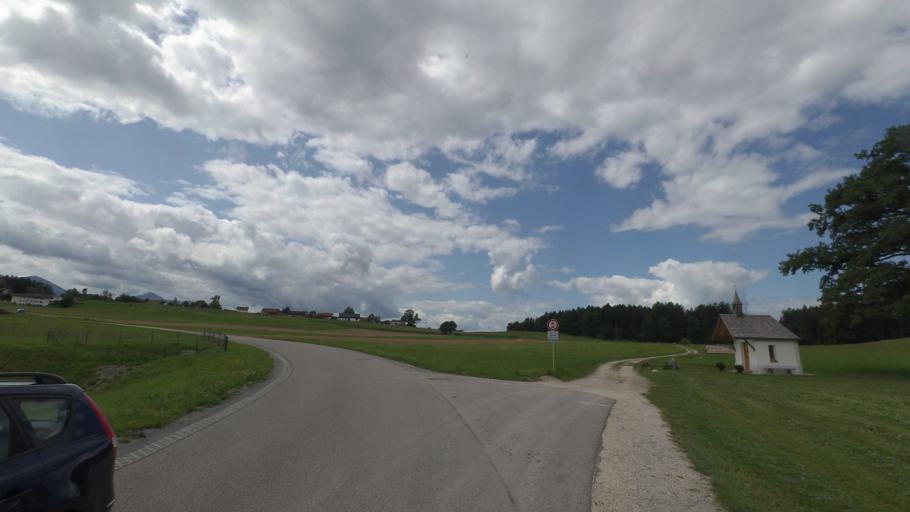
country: DE
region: Bavaria
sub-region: Upper Bavaria
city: Vachendorf
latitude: 47.8665
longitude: 12.6134
